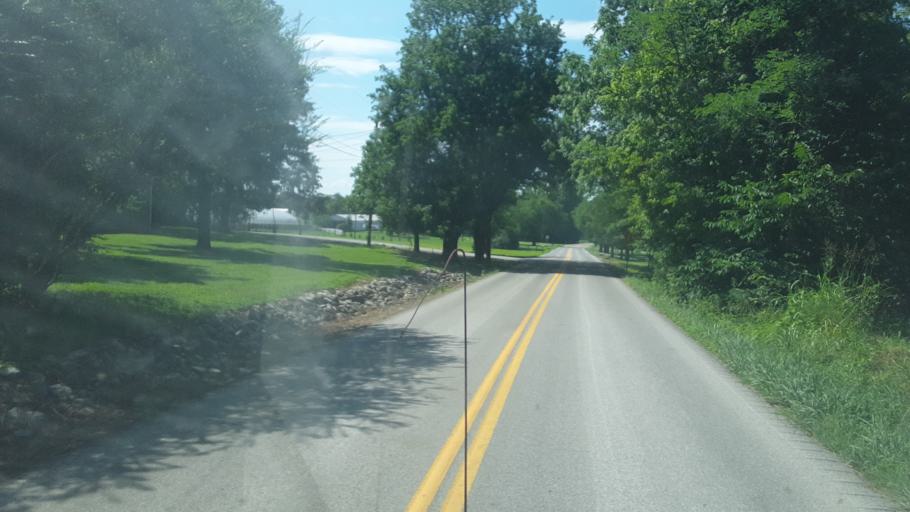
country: US
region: Kentucky
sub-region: Todd County
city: Elkton
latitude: 36.8412
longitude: -87.3008
